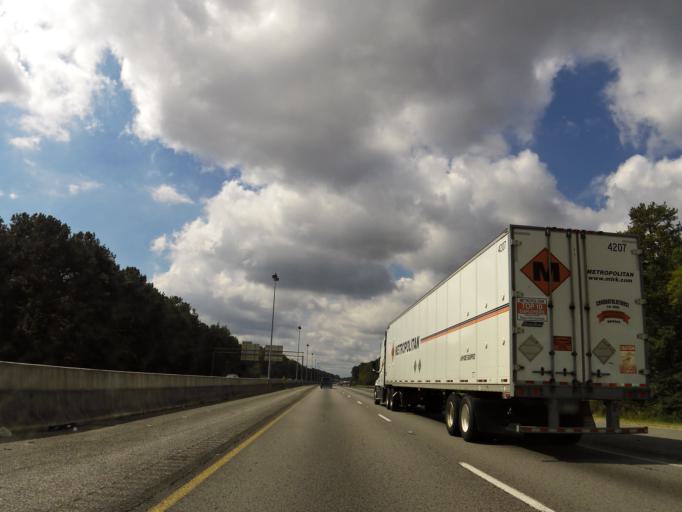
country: US
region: Alabama
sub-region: Jefferson County
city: Bessemer
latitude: 33.3381
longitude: -87.0326
